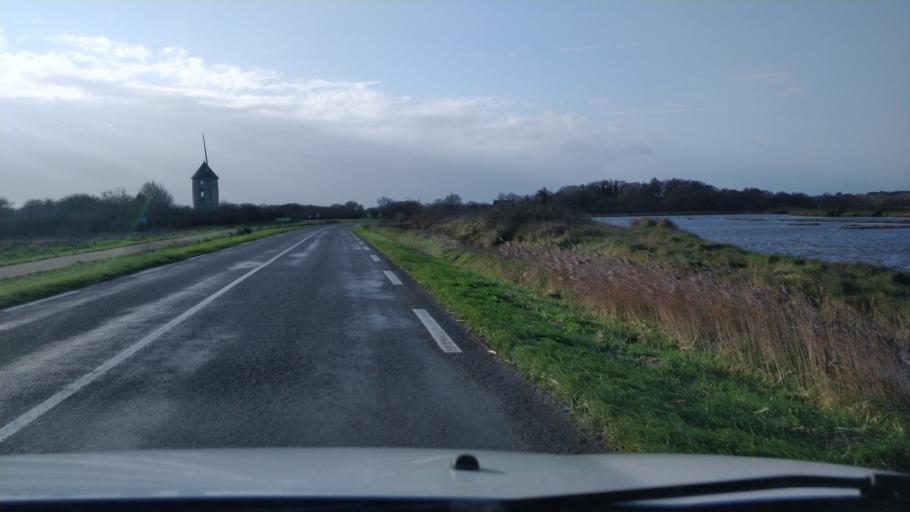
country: FR
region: Pays de la Loire
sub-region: Departement de la Loire-Atlantique
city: Asserac
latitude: 47.4070
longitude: -2.3991
